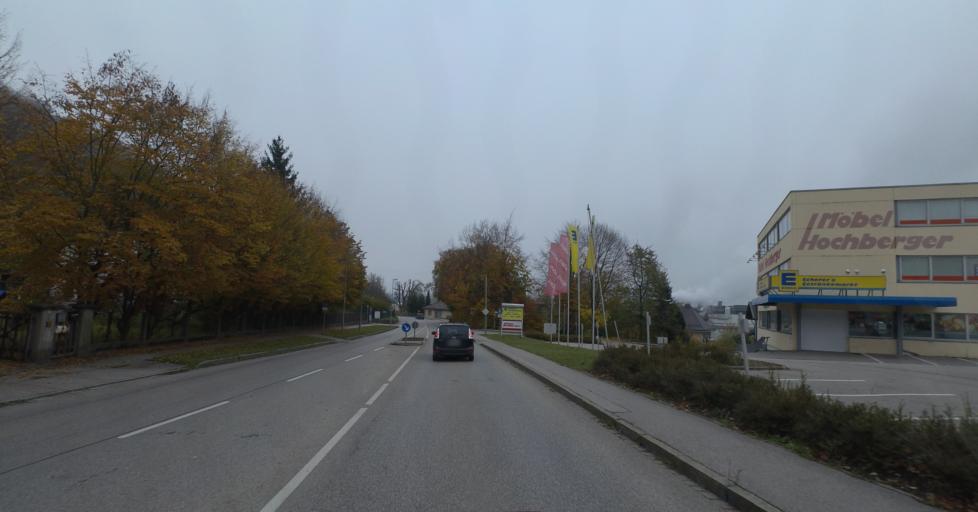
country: DE
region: Bavaria
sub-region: Upper Bavaria
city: Trostberg an der Alz
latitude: 48.0255
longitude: 12.5416
